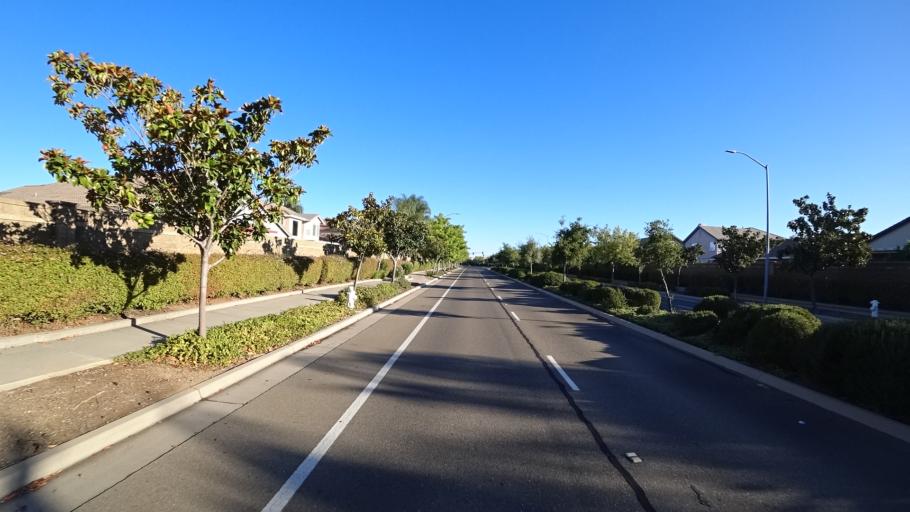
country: US
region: California
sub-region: Sacramento County
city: Laguna
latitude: 38.4425
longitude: -121.3921
